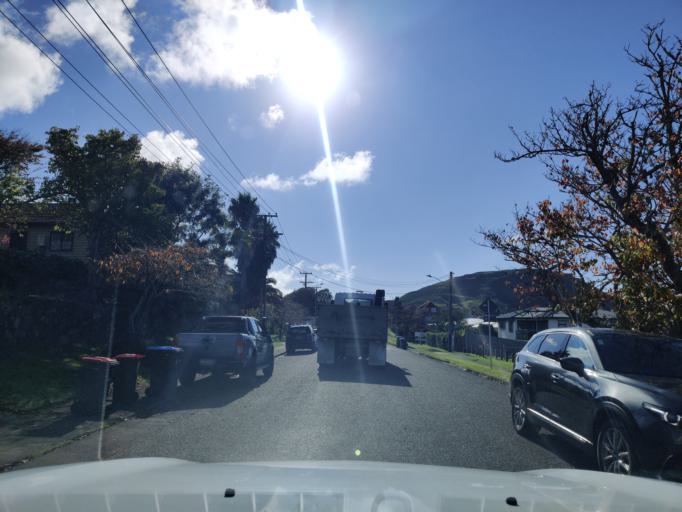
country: NZ
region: Auckland
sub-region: Auckland
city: Tamaki
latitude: -36.8988
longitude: 174.8394
